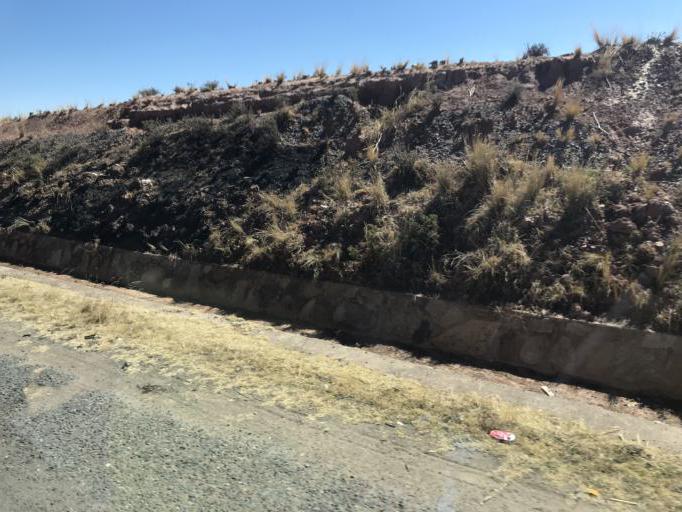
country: BO
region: La Paz
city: Tiahuanaco
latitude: -16.5943
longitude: -68.5780
